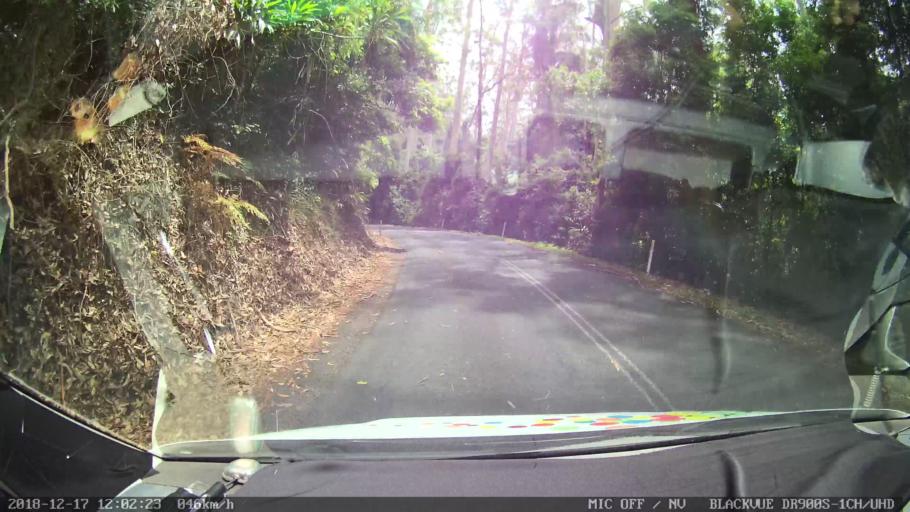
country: AU
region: New South Wales
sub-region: Kyogle
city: Kyogle
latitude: -28.5164
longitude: 152.5686
